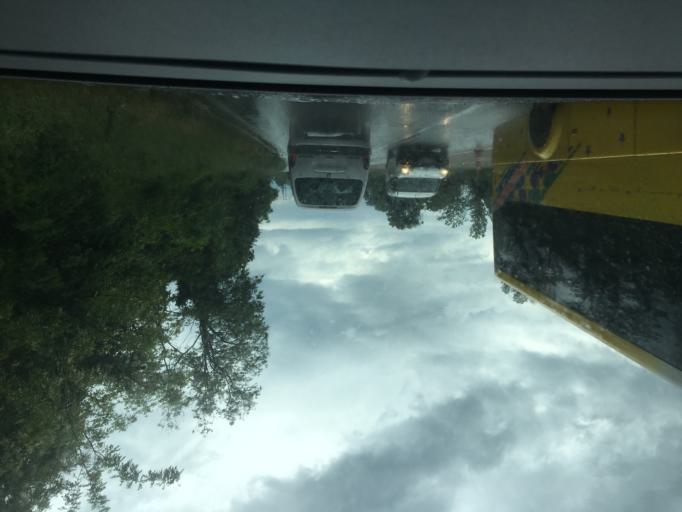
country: MK
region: Ohrid
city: Ohrid
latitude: 41.1422
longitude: 20.7611
